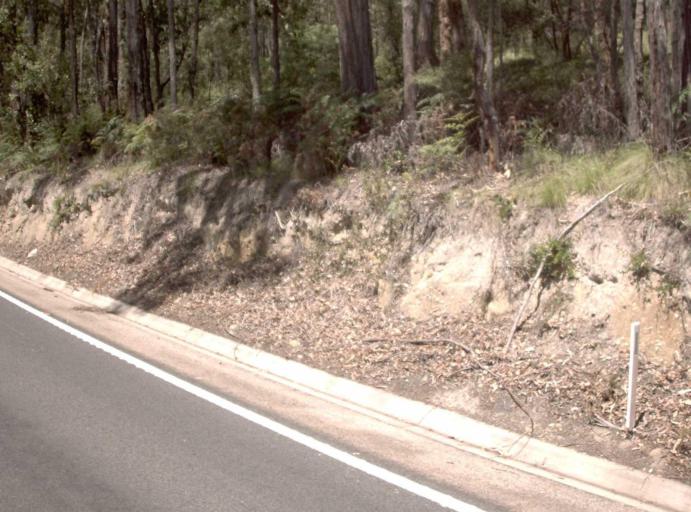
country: AU
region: Victoria
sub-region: East Gippsland
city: Lakes Entrance
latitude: -37.6948
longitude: 148.7242
